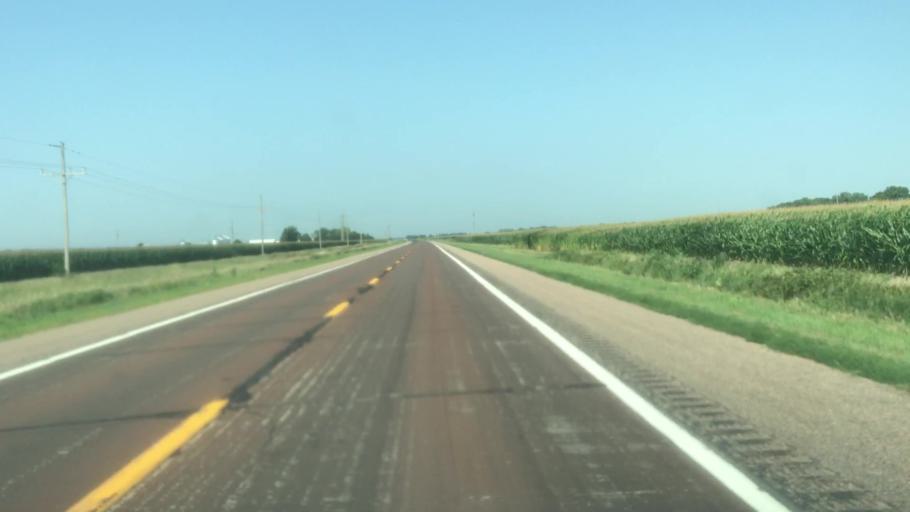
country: US
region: Nebraska
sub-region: Hall County
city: Grand Island
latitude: 40.9677
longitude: -98.4697
